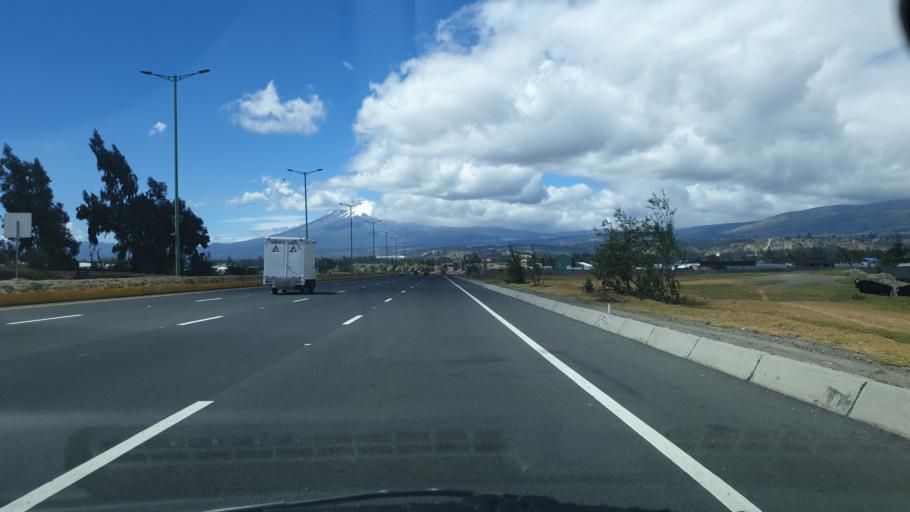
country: EC
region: Cotopaxi
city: Saquisili
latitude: -0.8737
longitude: -78.6420
